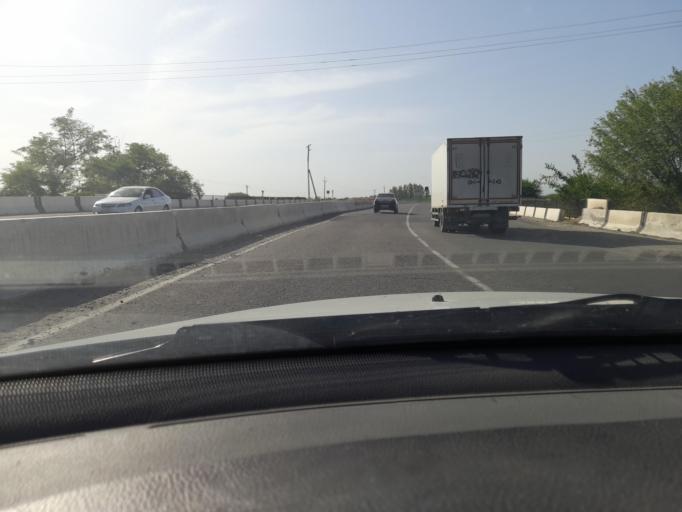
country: UZ
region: Samarqand
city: Kattaqo'rg'on
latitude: 39.9244
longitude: 66.2754
